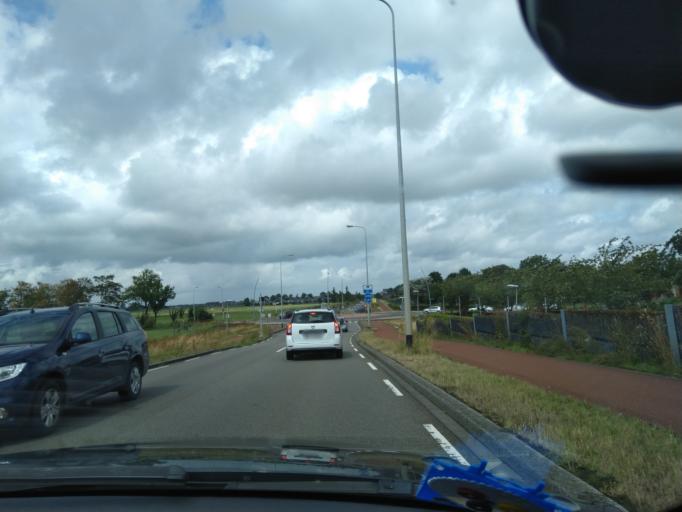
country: NL
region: Groningen
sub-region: Gemeente Groningen
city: Groningen
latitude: 53.2154
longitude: 6.5129
